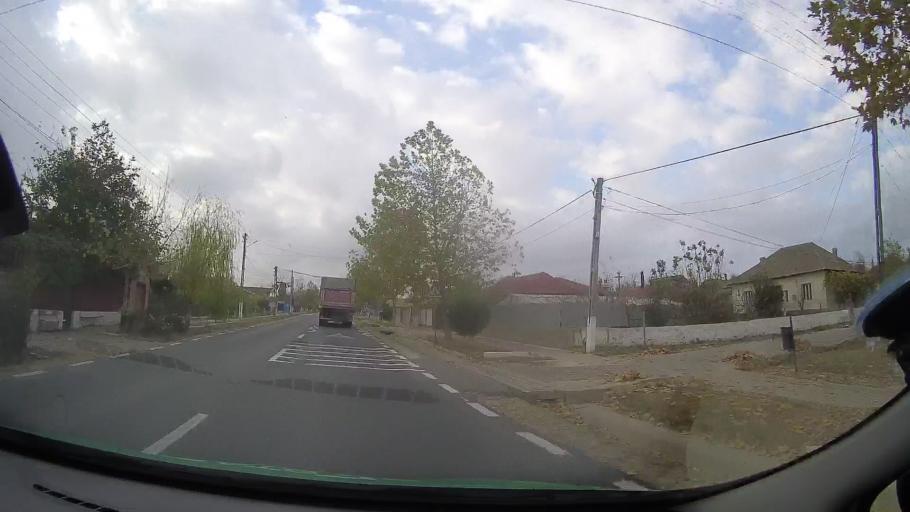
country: RO
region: Constanta
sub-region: Comuna Mircea Voda
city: Satu Nou
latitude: 44.2686
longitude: 28.2211
